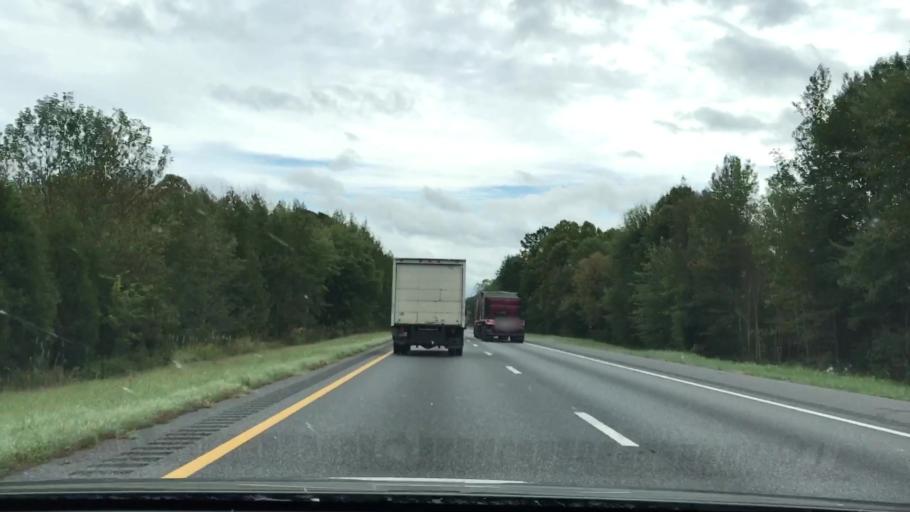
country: US
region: Kentucky
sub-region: Todd County
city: Guthrie
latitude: 36.4995
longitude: -87.1824
